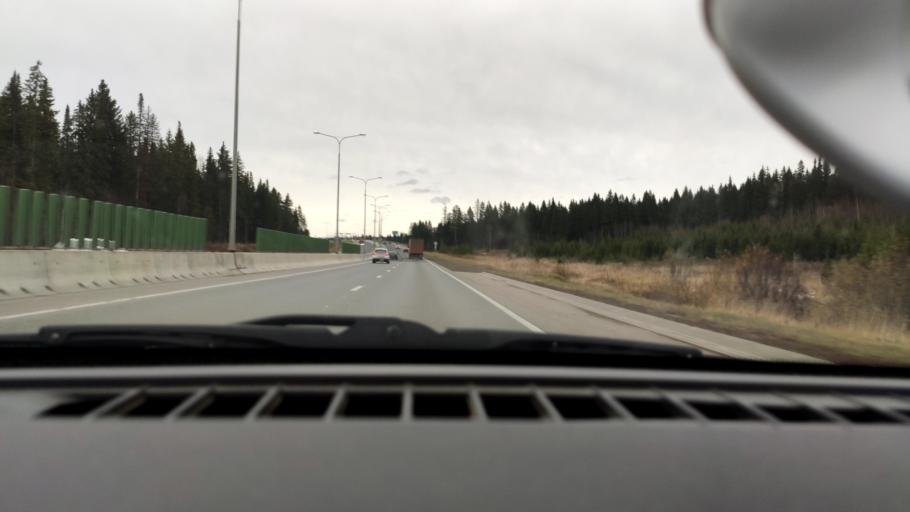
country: RU
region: Perm
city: Ferma
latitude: 57.9447
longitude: 56.3815
